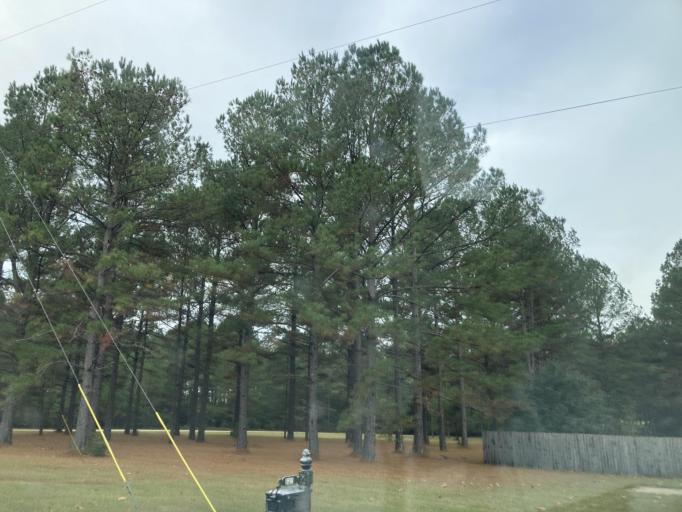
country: US
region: Mississippi
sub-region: Lamar County
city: Purvis
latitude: 31.1153
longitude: -89.4676
